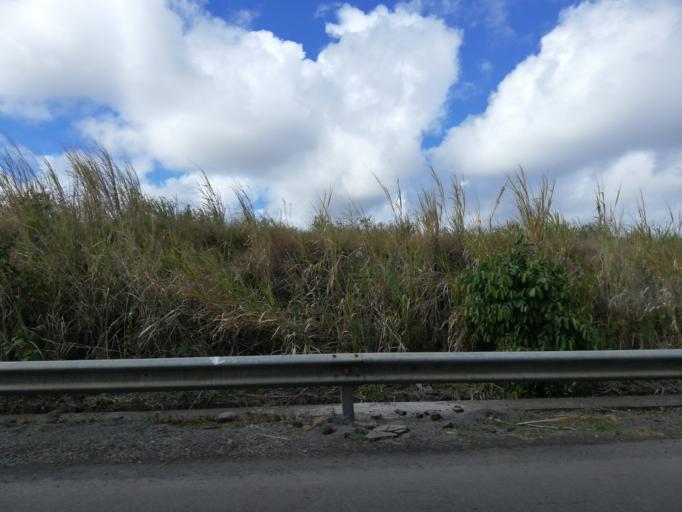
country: MU
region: Grand Port
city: Plaine Magnien
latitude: -20.4274
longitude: 57.6521
